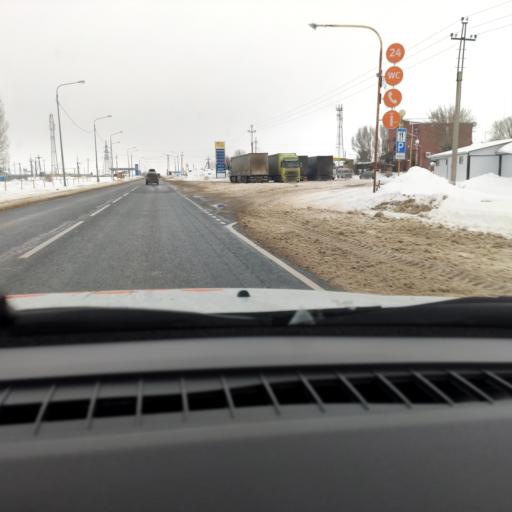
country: RU
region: Saratov
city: Perelyub
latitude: 52.2418
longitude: 50.7308
